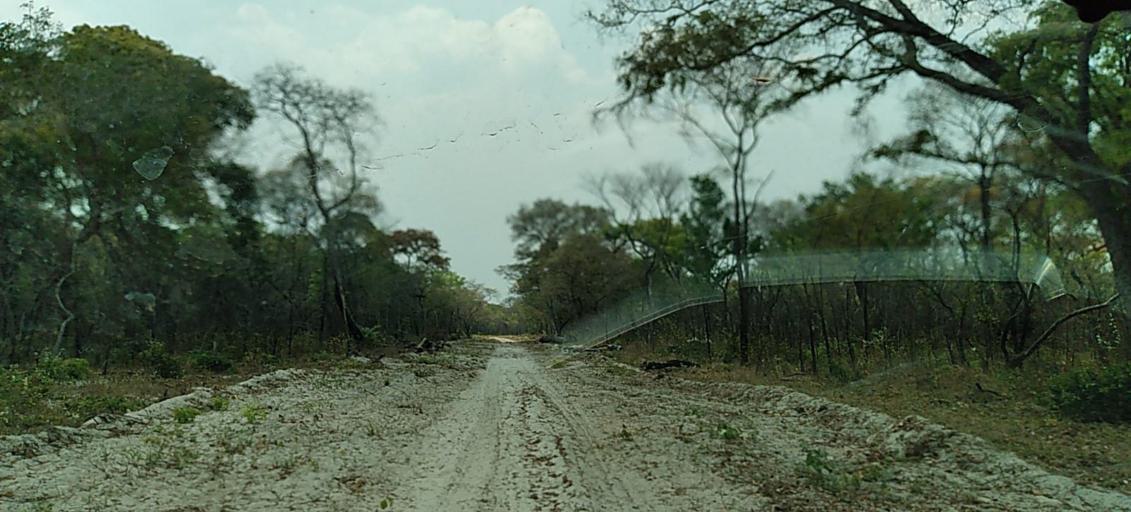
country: ZM
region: Western
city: Lukulu
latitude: -14.0079
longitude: 23.5832
